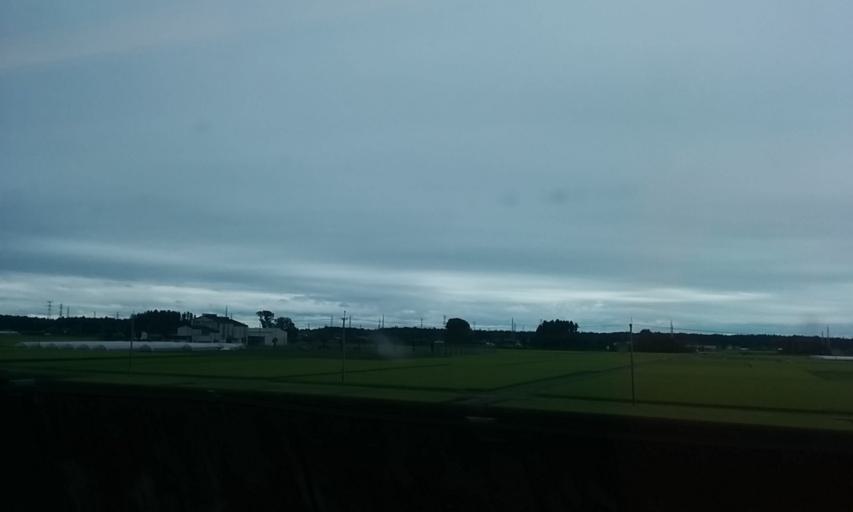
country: JP
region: Tochigi
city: Ujiie
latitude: 36.6427
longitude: 139.9112
